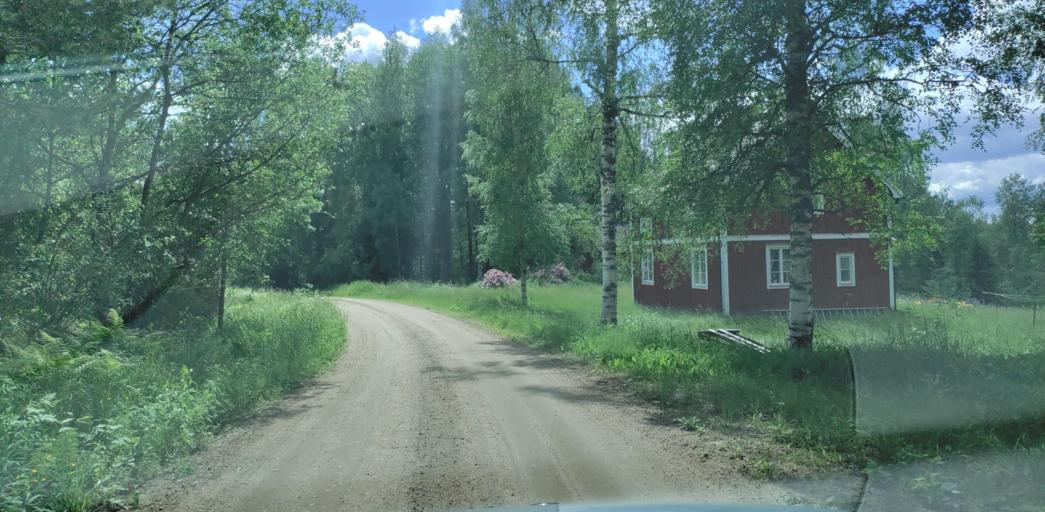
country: SE
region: Vaermland
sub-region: Hagfors Kommun
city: Ekshaerad
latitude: 60.0976
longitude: 13.3169
